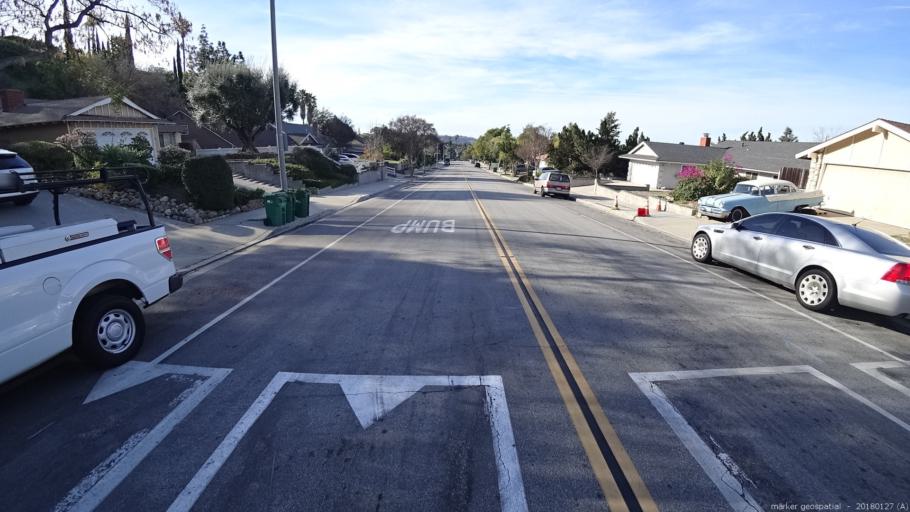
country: US
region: California
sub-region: Los Angeles County
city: Diamond Bar
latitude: 34.0322
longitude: -117.8062
